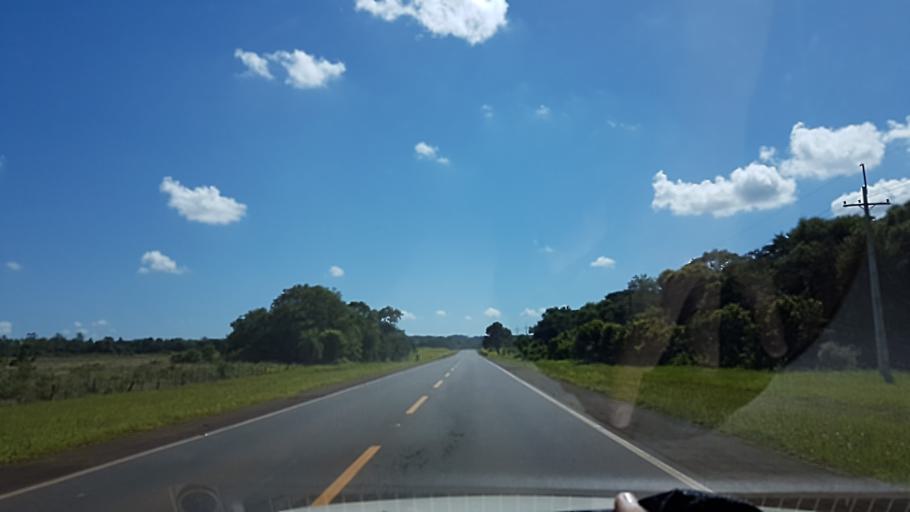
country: PY
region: Itapua
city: Carmen del Parana
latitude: -27.2159
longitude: -56.0924
